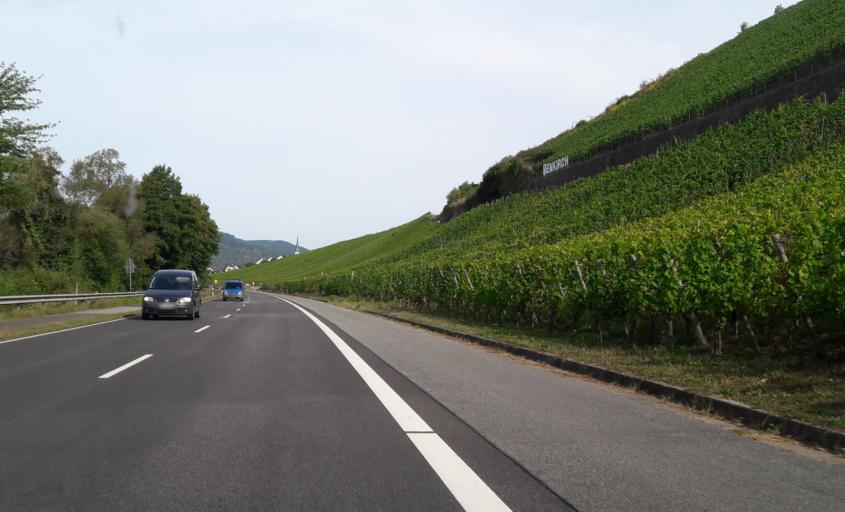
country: DE
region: Rheinland-Pfalz
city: Starkenburg
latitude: 49.9713
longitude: 7.1335
